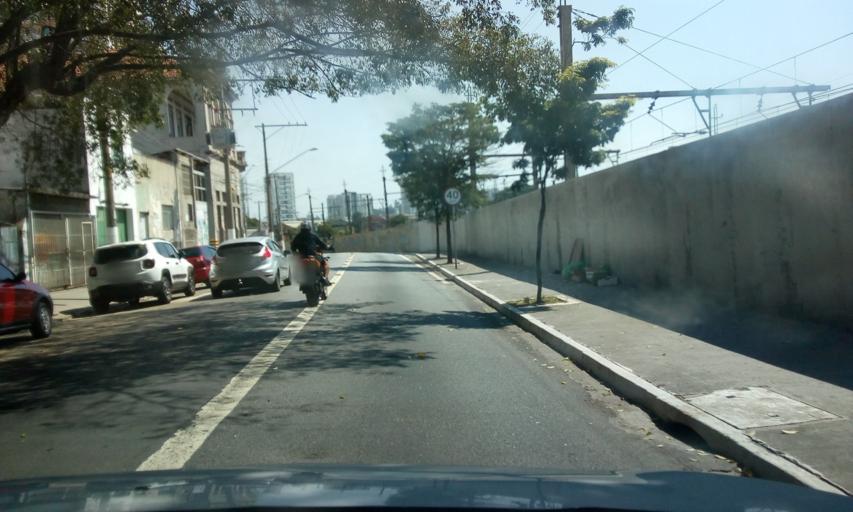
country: BR
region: Sao Paulo
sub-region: Sao Paulo
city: Sao Paulo
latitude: -23.5176
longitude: -46.7047
